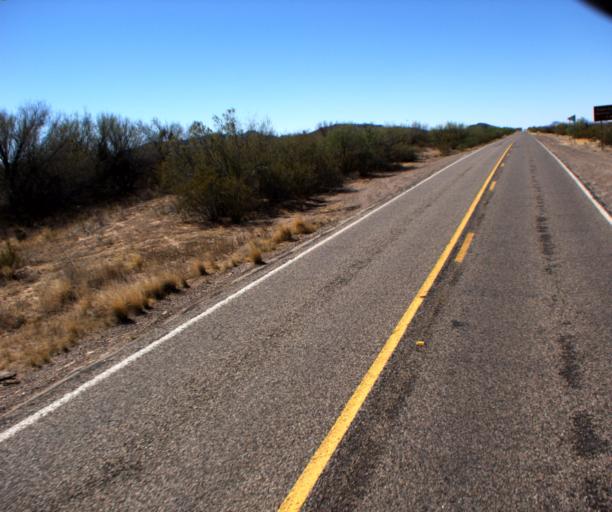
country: US
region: Arizona
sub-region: Pima County
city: Ajo
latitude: 32.2564
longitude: -112.7434
